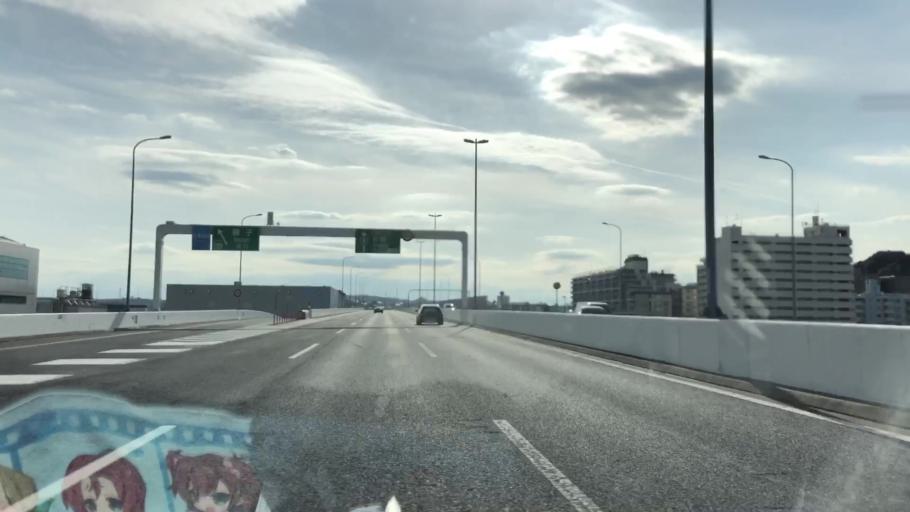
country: JP
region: Kanagawa
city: Yokohama
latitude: 35.4008
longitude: 139.6197
